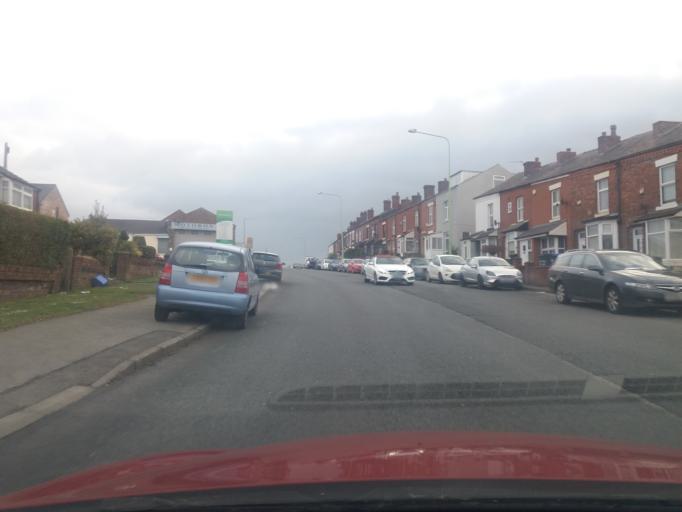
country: GB
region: England
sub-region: Lancashire
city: Chorley
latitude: 53.6632
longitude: -2.6180
